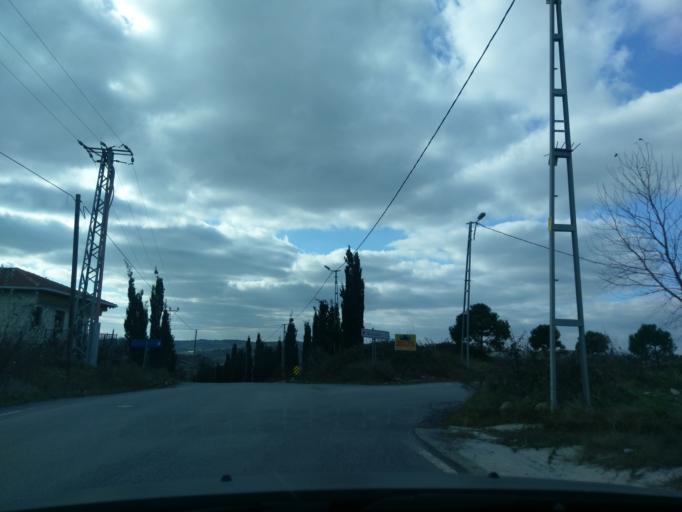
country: TR
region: Istanbul
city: Durusu
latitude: 41.3080
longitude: 28.6879
